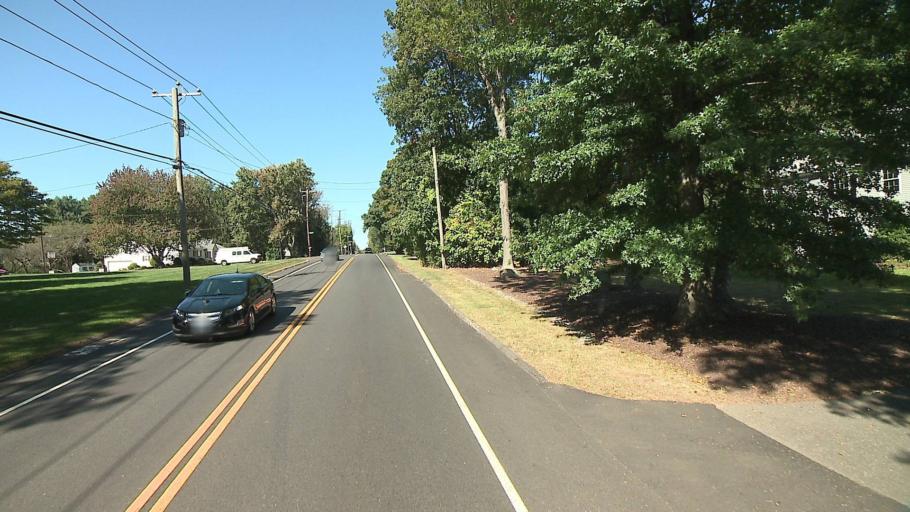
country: US
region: Connecticut
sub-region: New Haven County
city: Orange
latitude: 41.2804
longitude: -73.0086
